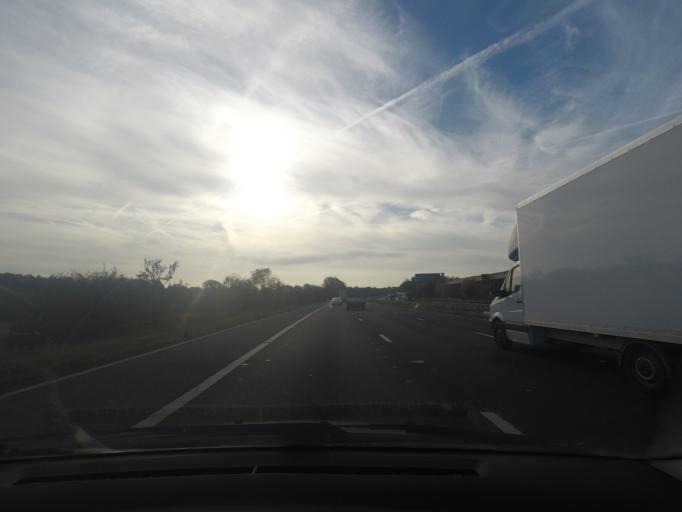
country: GB
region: England
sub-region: Barnsley
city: Darton
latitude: 53.5921
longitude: -1.5386
